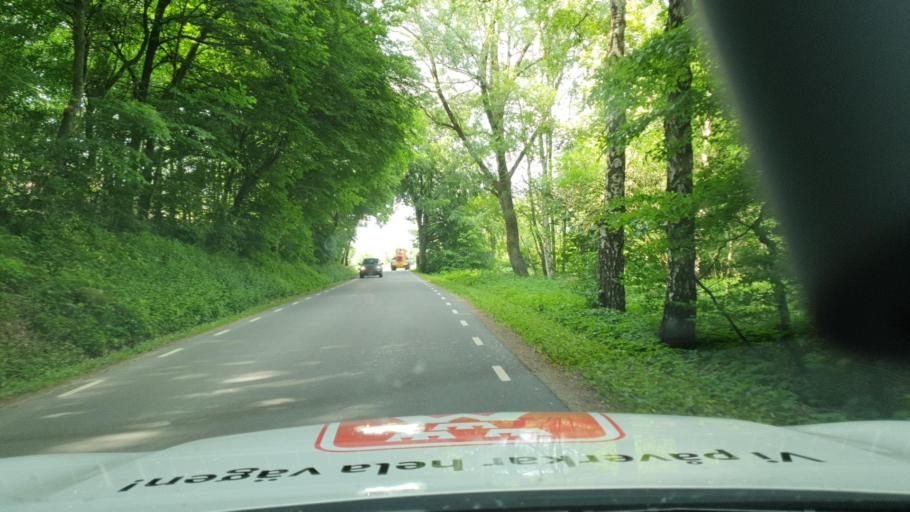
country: SE
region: Skane
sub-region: Skurups Kommun
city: Rydsgard
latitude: 55.5227
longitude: 13.5509
